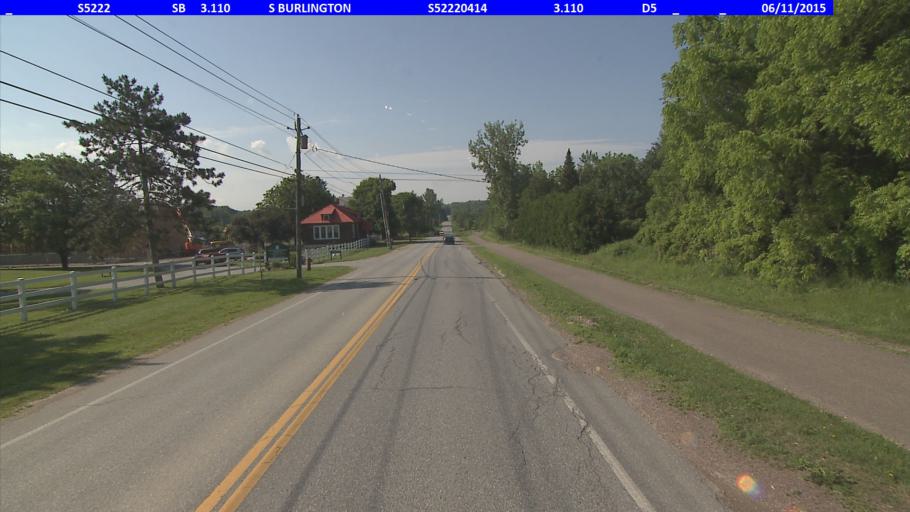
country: US
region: Vermont
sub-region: Chittenden County
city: South Burlington
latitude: 44.4611
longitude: -73.1904
